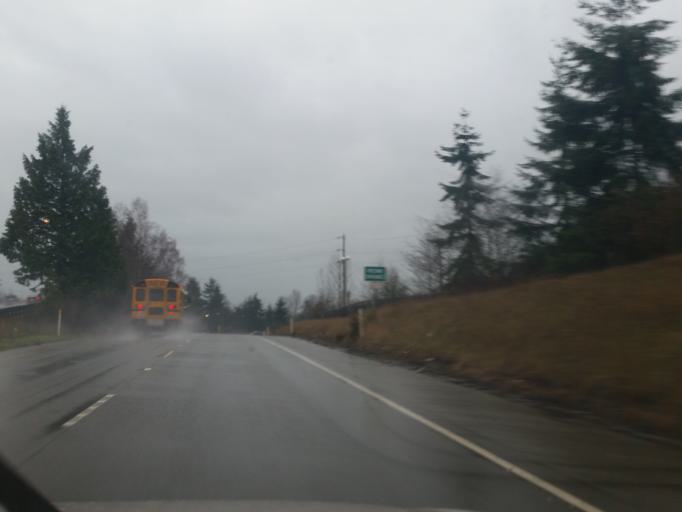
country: US
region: Washington
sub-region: Snohomish County
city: Mukilteo
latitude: 47.9242
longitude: -122.2610
